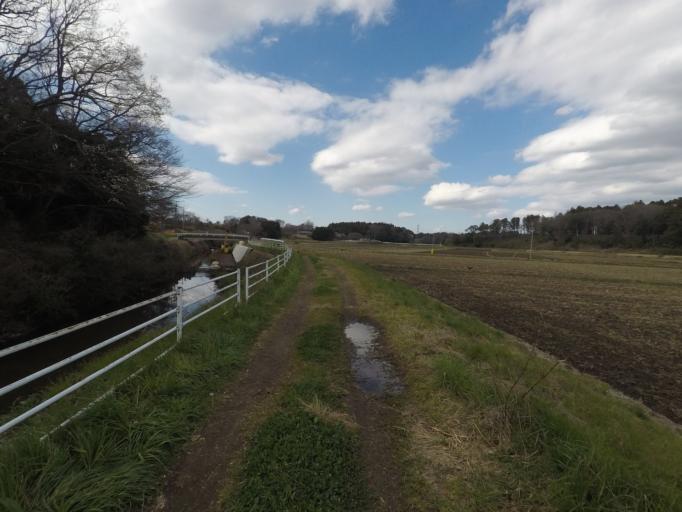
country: JP
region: Ibaraki
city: Ushiku
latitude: 35.9907
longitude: 140.1189
